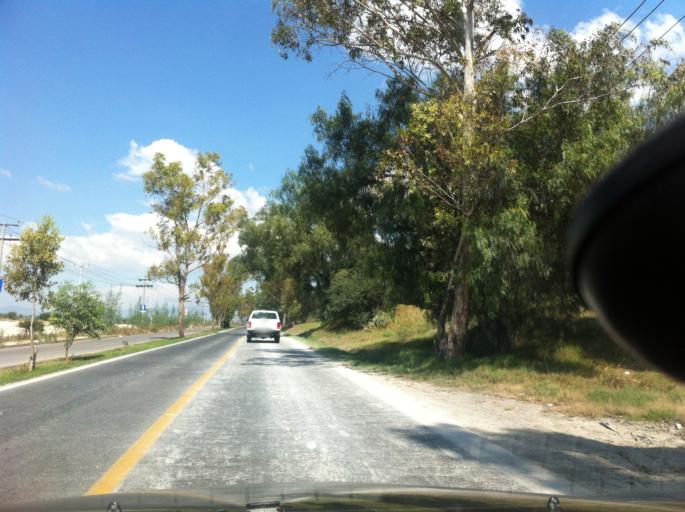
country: MX
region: Mexico
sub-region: Zumpango
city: Zumpango
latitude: 19.7881
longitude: -99.1175
